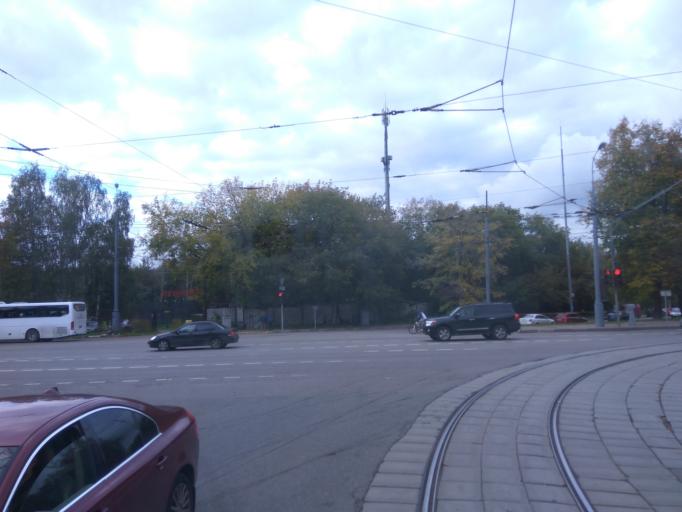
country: RU
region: Moscow
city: Metrogorodok
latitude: 55.7882
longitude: 37.7623
